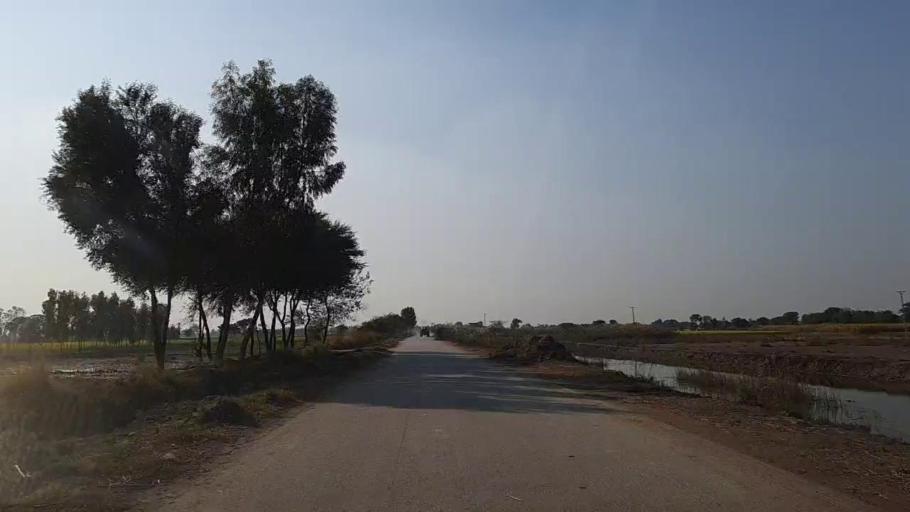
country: PK
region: Sindh
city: Daur
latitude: 26.4042
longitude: 68.2717
